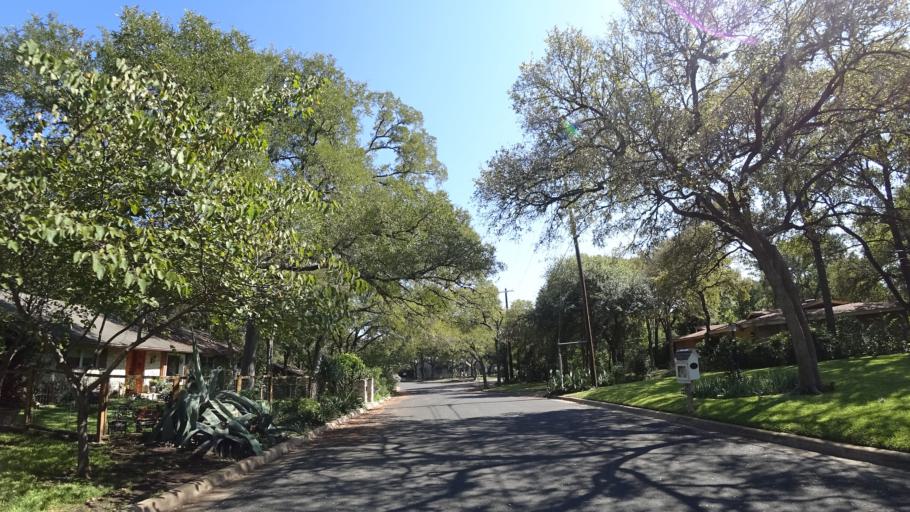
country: US
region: Texas
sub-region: Travis County
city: Rollingwood
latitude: 30.2472
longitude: -97.7880
